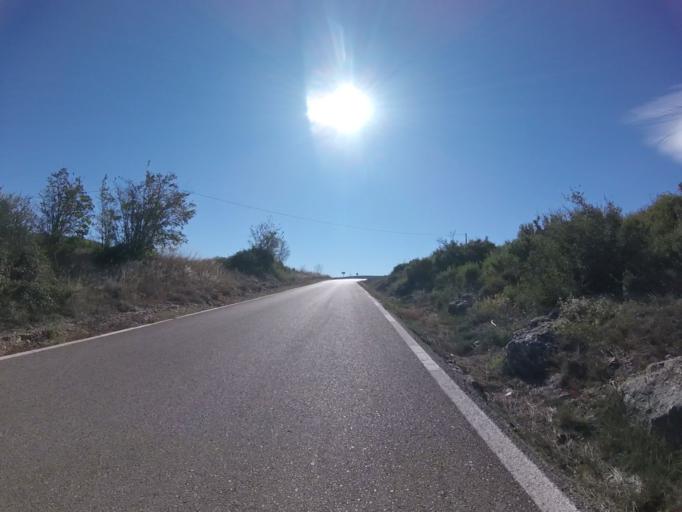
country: ES
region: Valencia
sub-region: Provincia de Castello
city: Albocasser
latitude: 40.3745
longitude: 0.0196
